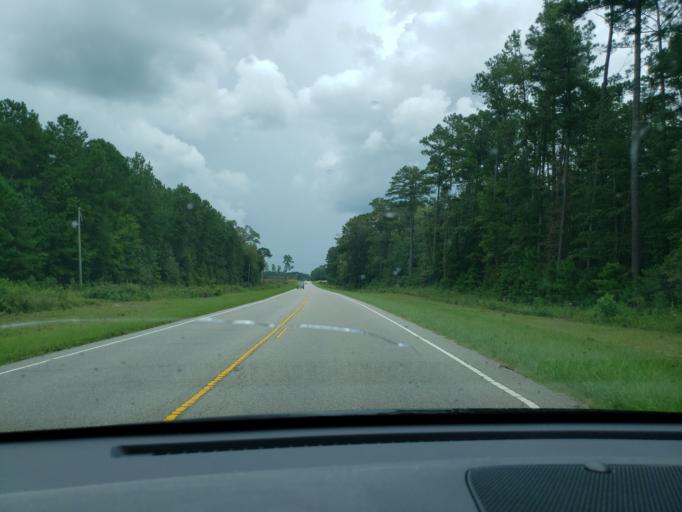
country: US
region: North Carolina
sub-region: Bladen County
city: Bladenboro
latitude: 34.4712
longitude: -78.6689
